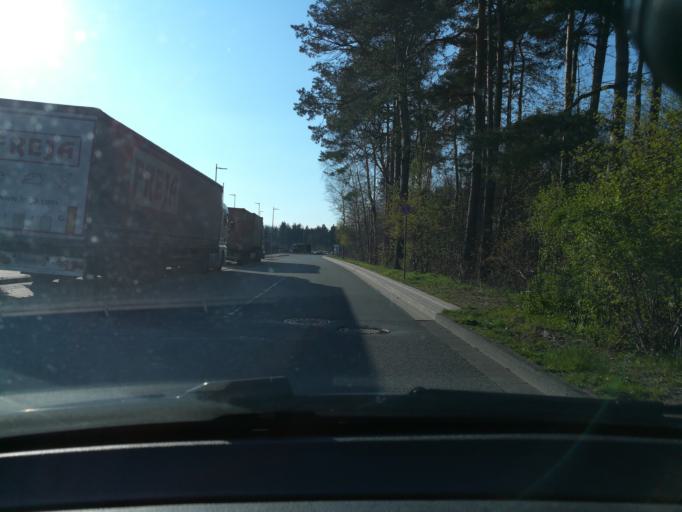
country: DE
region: North Rhine-Westphalia
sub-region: Regierungsbezirk Detmold
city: Verl
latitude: 51.9448
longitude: 8.5636
